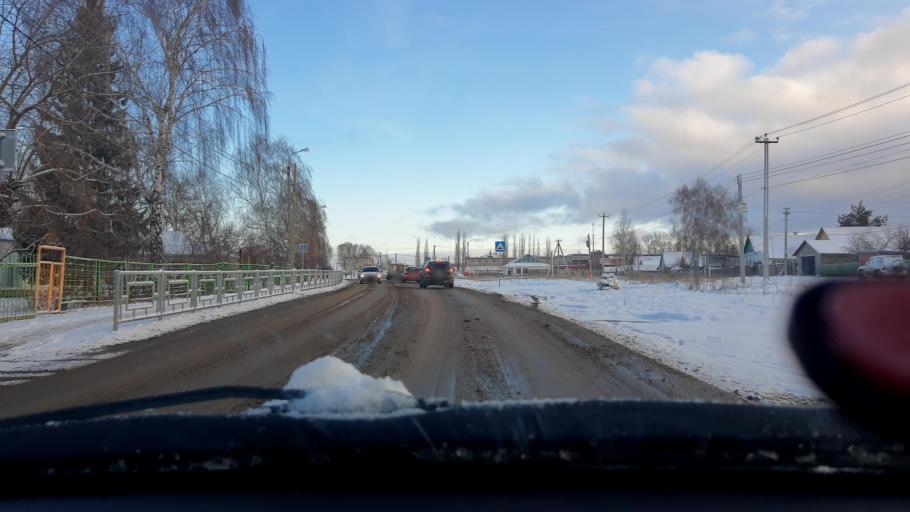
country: RU
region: Bashkortostan
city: Iglino
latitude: 54.7865
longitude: 56.2292
